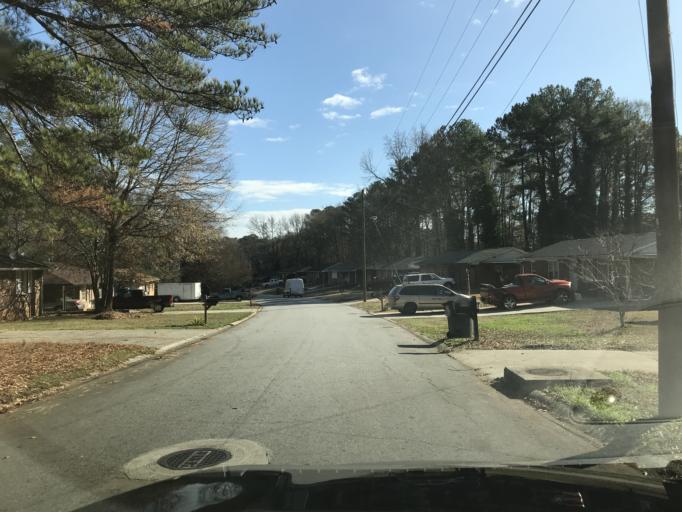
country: US
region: Georgia
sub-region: Clayton County
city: Forest Park
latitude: 33.5881
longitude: -84.3756
